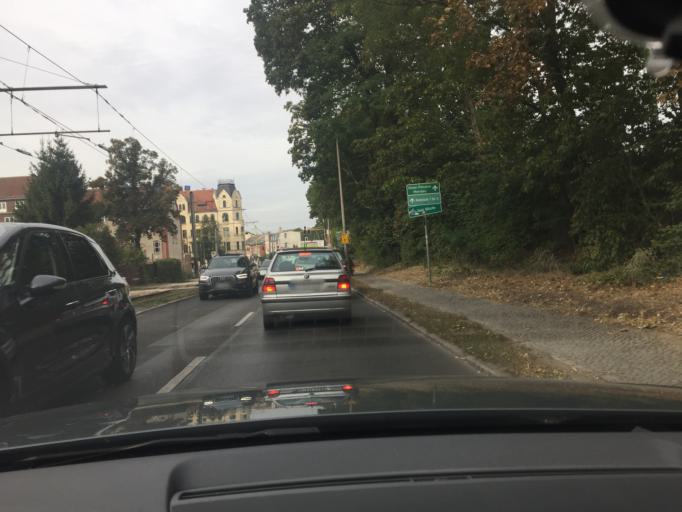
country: DE
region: Berlin
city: Friedrichshagen
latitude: 52.4570
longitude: 13.6274
